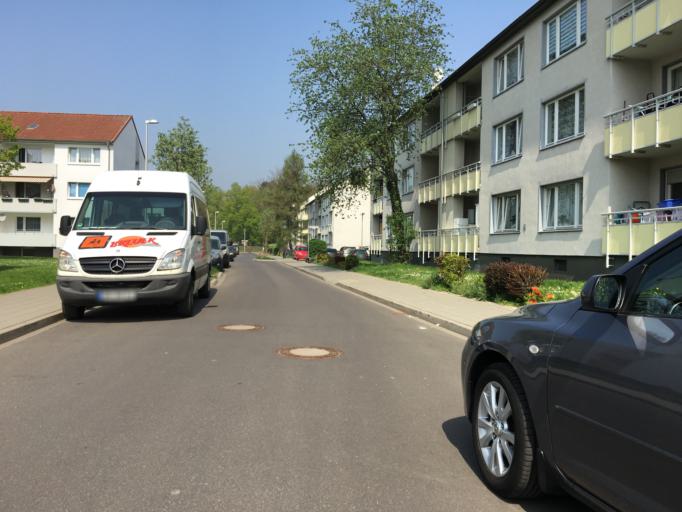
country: DE
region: North Rhine-Westphalia
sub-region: Regierungsbezirk Koln
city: Dueren
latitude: 50.8030
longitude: 6.5050
